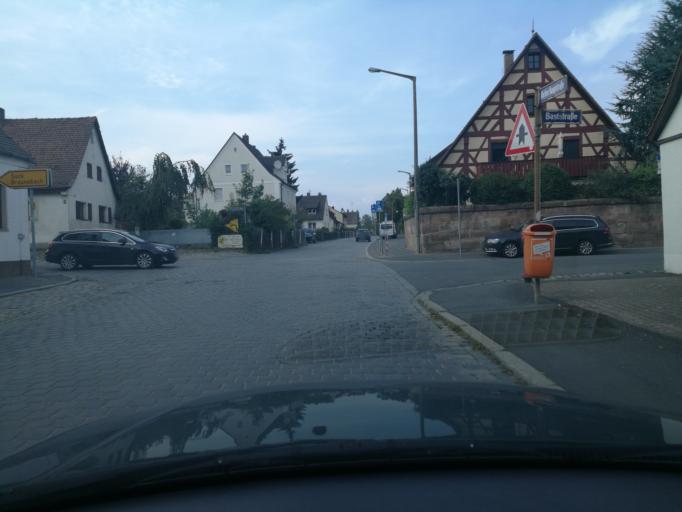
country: DE
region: Bavaria
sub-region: Regierungsbezirk Mittelfranken
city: Wetzendorf
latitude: 49.4989
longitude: 11.0440
